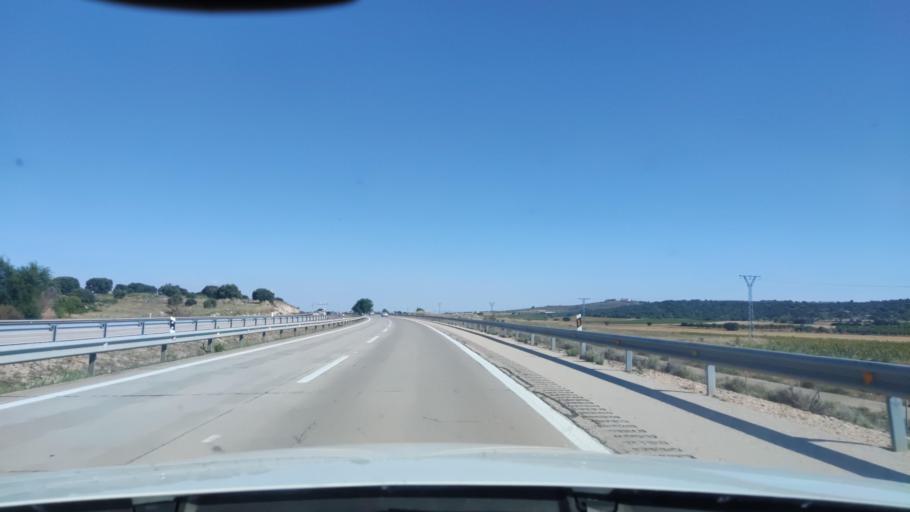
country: ES
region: Castille-La Mancha
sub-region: Provincia de Cuenca
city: Sisante
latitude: 39.3964
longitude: -2.2129
